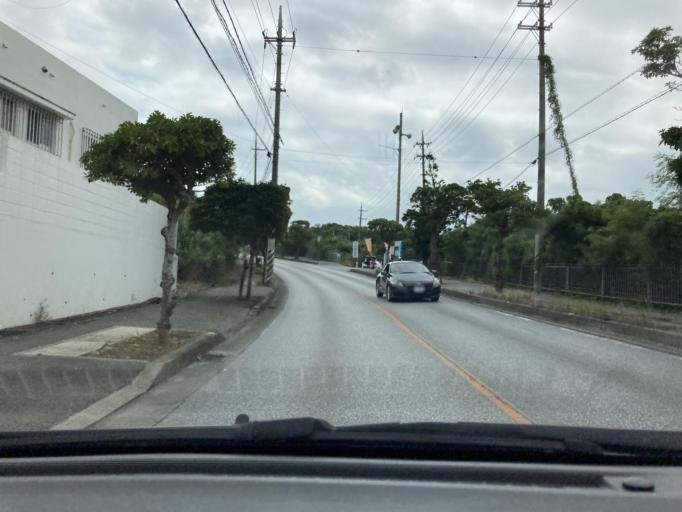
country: JP
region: Okinawa
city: Ginowan
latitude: 26.2600
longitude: 127.7766
